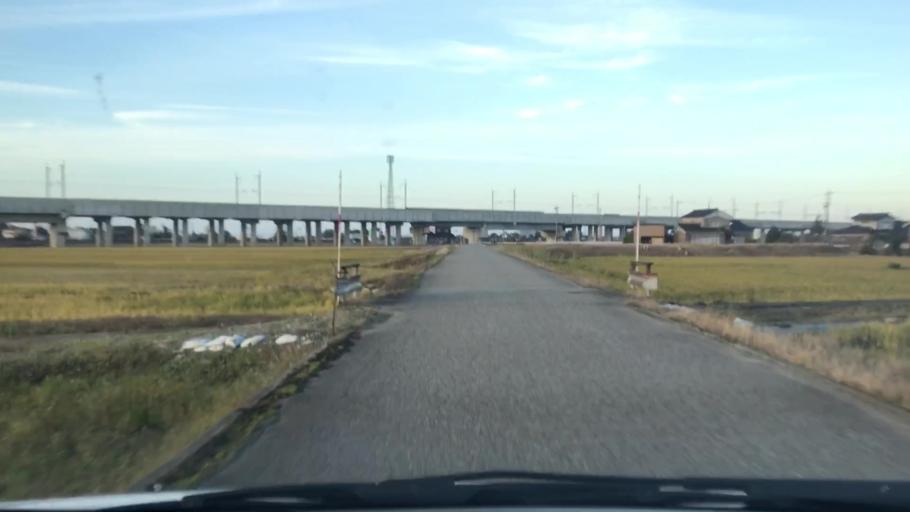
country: JP
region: Toyama
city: Namerikawa
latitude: 36.7297
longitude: 137.3357
